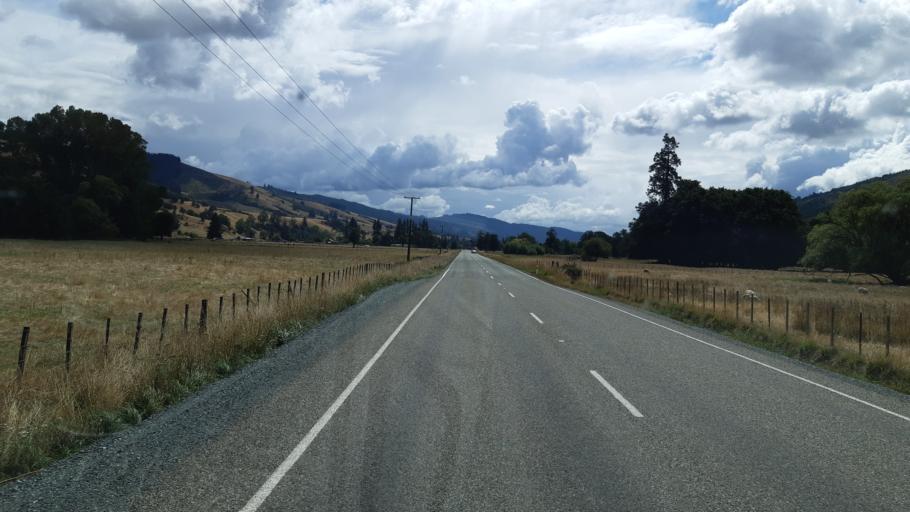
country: NZ
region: Tasman
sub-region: Tasman District
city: Wakefield
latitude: -41.5265
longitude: 172.7957
